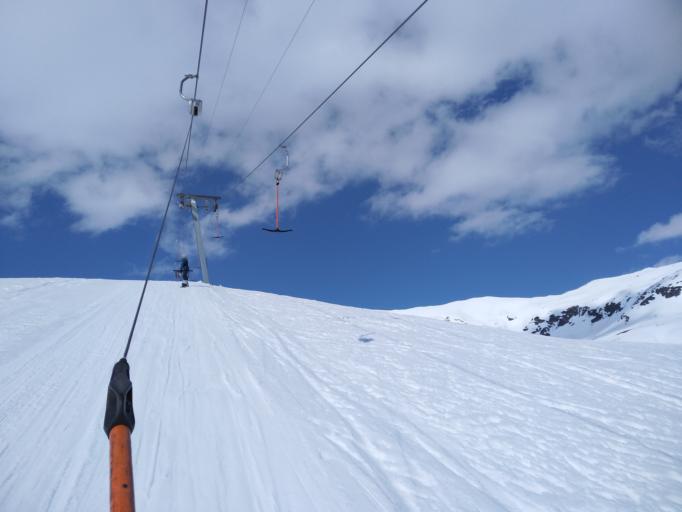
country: NO
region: Sogn og Fjordane
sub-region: Vik
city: Vik
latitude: 60.8655
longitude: 6.4573
